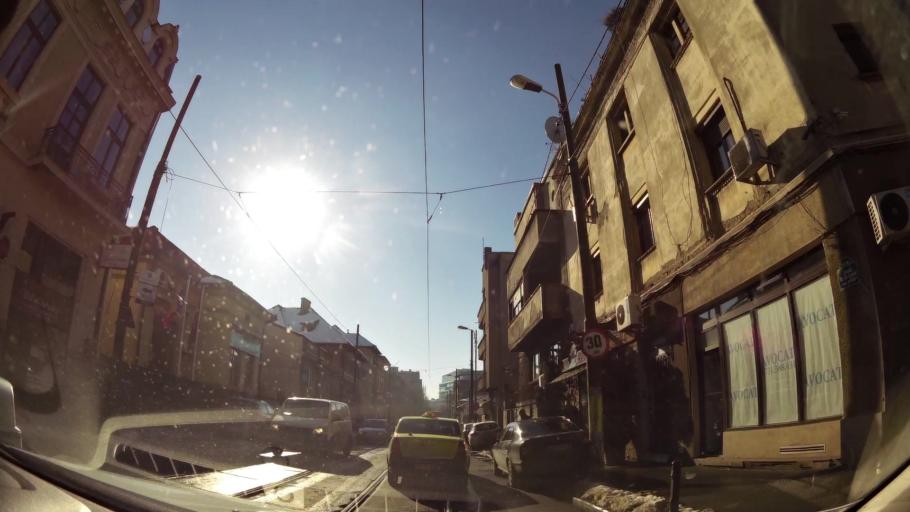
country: RO
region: Bucuresti
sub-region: Municipiul Bucuresti
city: Bucharest
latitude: 44.4439
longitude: 26.1105
